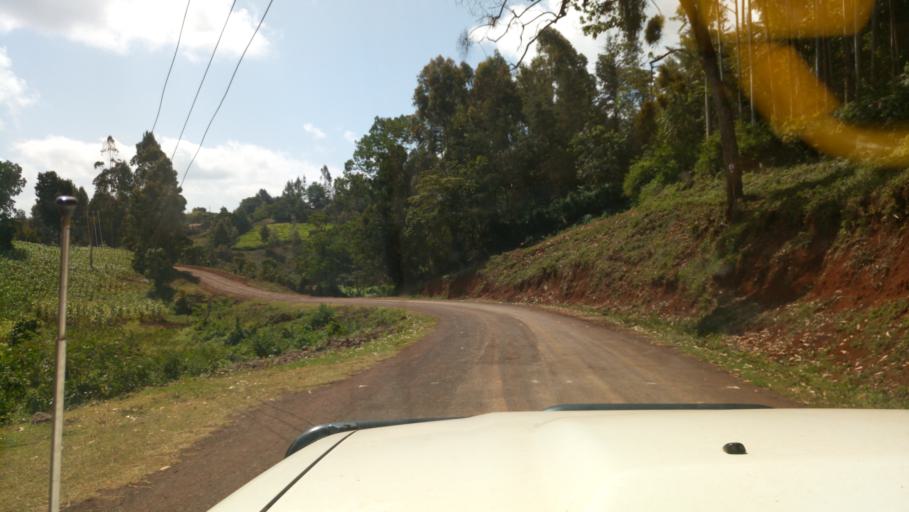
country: KE
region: Nyeri
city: Nyeri
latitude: -0.4075
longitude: 36.8894
